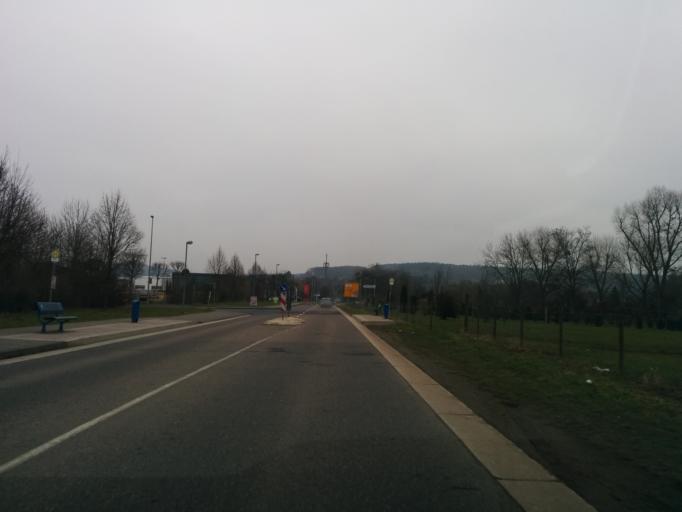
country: DE
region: Rheinland-Pfalz
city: Urbar
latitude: 50.3714
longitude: 7.6420
